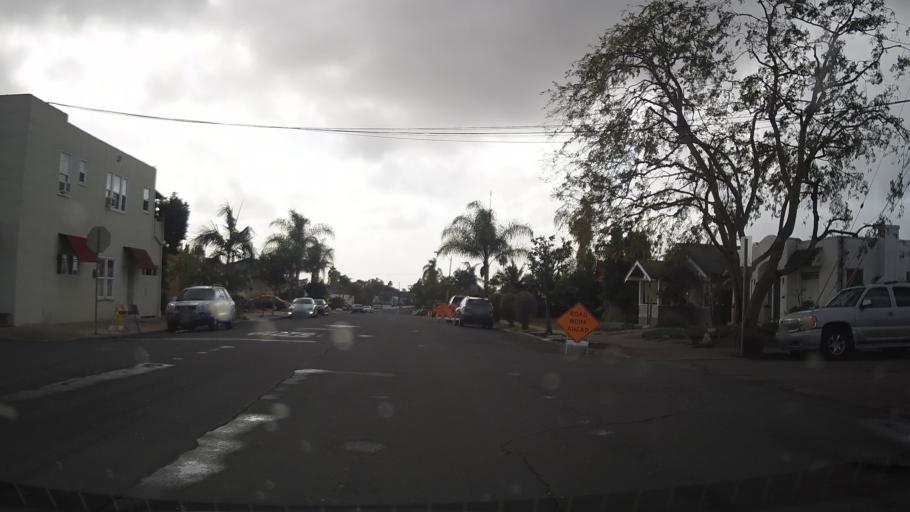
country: US
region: California
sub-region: San Diego County
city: San Diego
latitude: 32.7439
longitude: -117.1218
